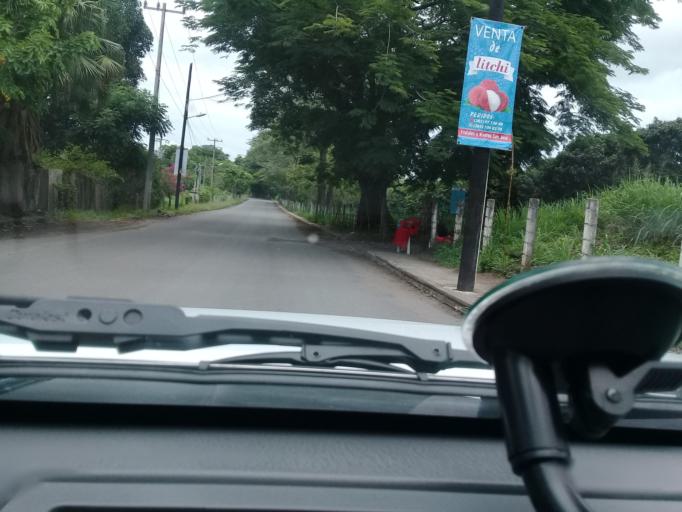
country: MX
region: Veracruz
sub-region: Paso de Ovejas
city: El Hatito
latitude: 19.2730
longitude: -96.3993
